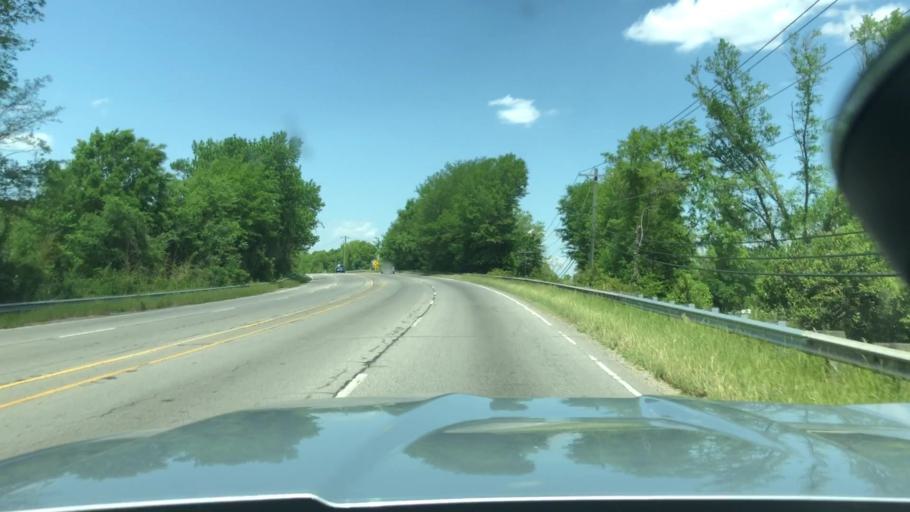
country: US
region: South Carolina
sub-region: Lexington County
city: Pineridge
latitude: 33.9073
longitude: -81.0660
